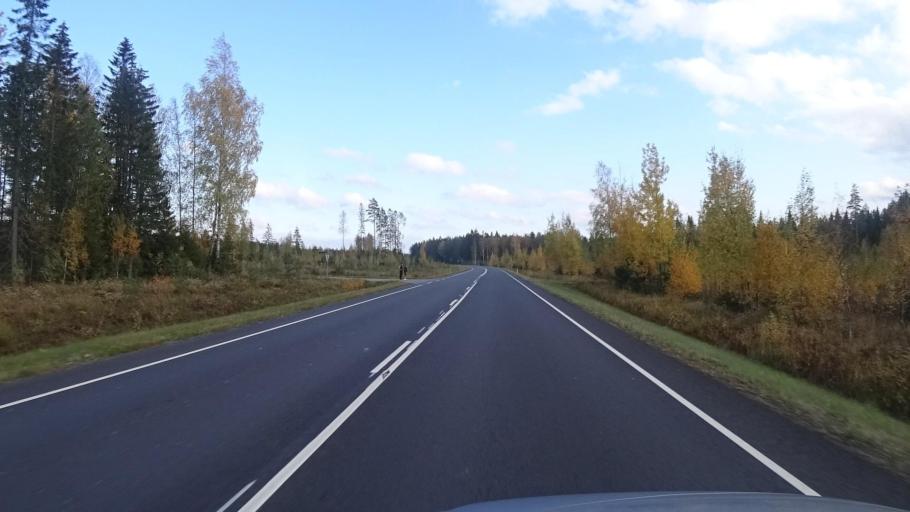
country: FI
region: Satakunta
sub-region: Rauma
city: Eura
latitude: 61.1092
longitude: 22.2111
